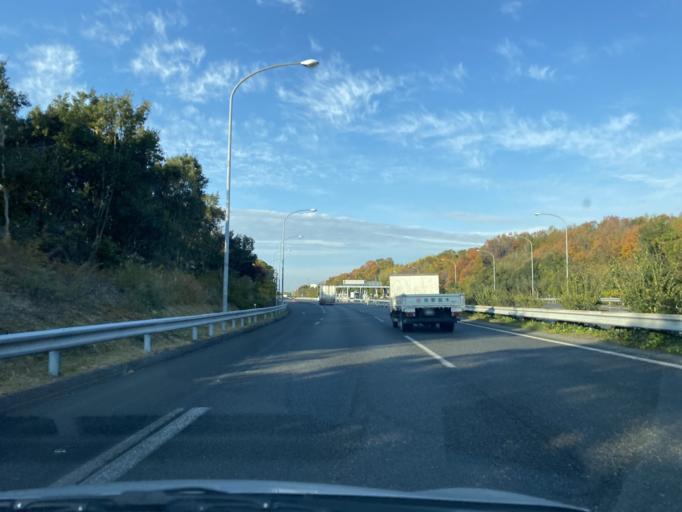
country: JP
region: Osaka
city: Izumi
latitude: 34.4246
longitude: 135.4484
